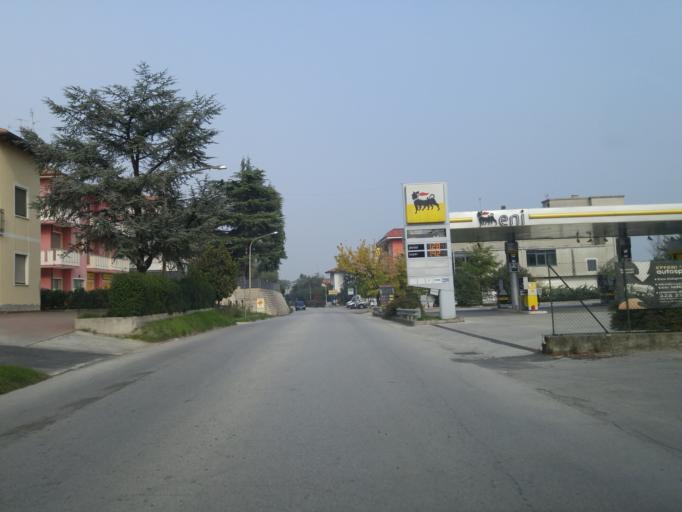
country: IT
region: The Marches
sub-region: Provincia di Pesaro e Urbino
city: Calcinelli
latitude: 43.7536
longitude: 12.9211
